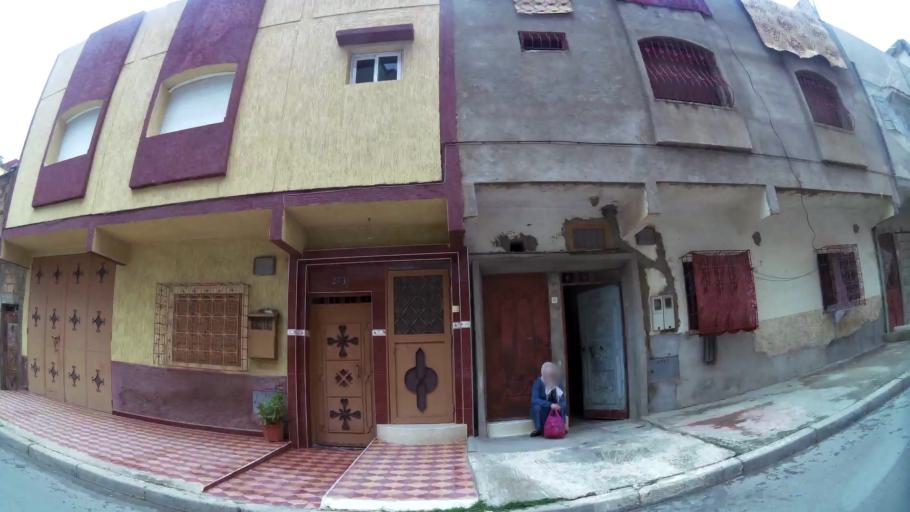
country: MA
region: Rabat-Sale-Zemmour-Zaer
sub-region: Khemisset
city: Tiflet
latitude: 33.8857
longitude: -6.3199
